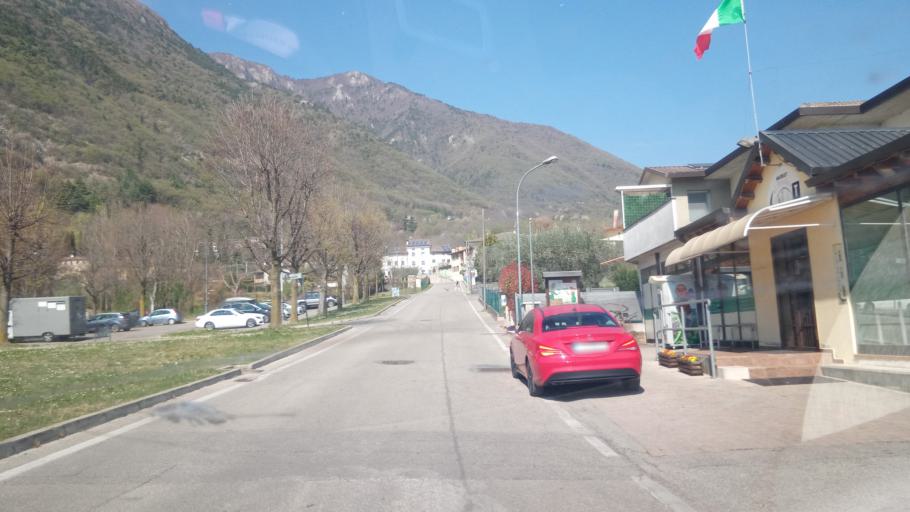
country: IT
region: Veneto
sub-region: Provincia di Treviso
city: Borso del Grappa
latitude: 45.8101
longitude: 11.7727
